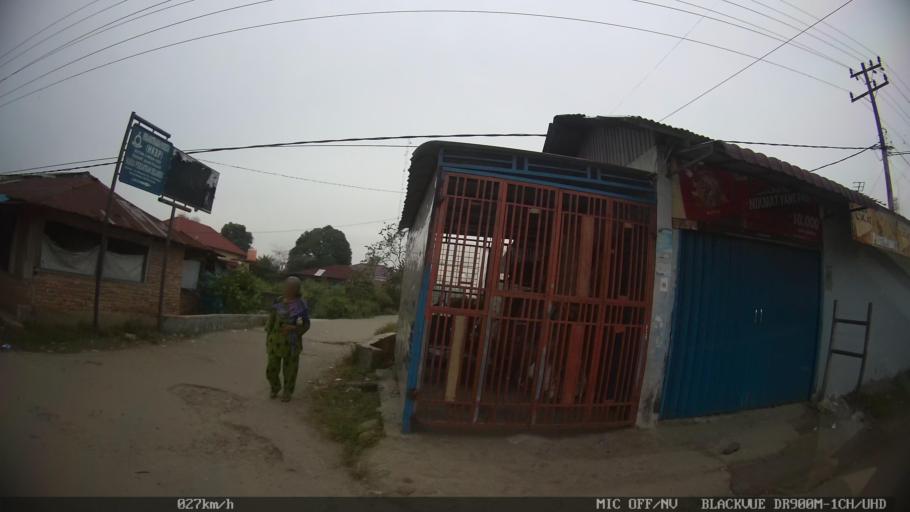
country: ID
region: North Sumatra
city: Deli Tua
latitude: 3.5510
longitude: 98.7226
